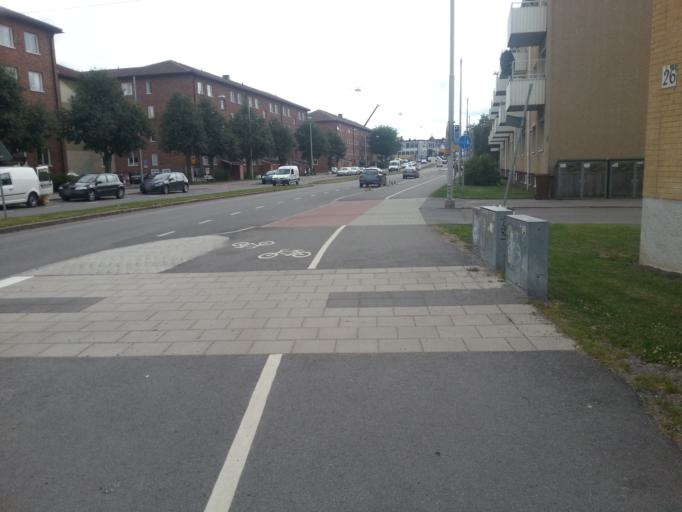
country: SE
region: OEstergoetland
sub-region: Norrkopings Kommun
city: Norrkoping
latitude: 58.5824
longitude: 16.1984
